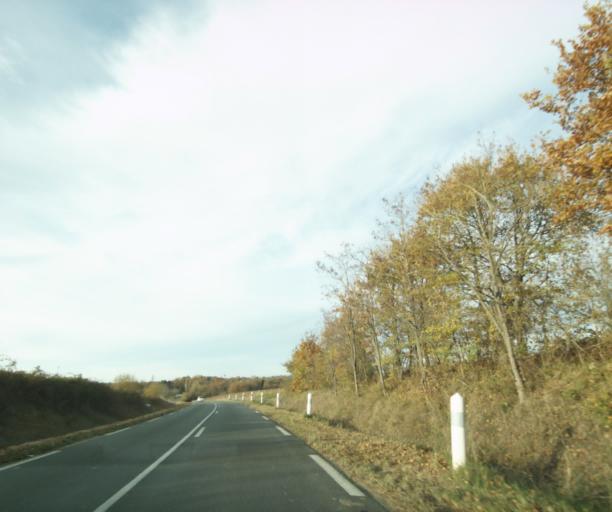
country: FR
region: Midi-Pyrenees
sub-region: Departement du Gers
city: Eauze
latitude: 43.8262
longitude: 0.0952
